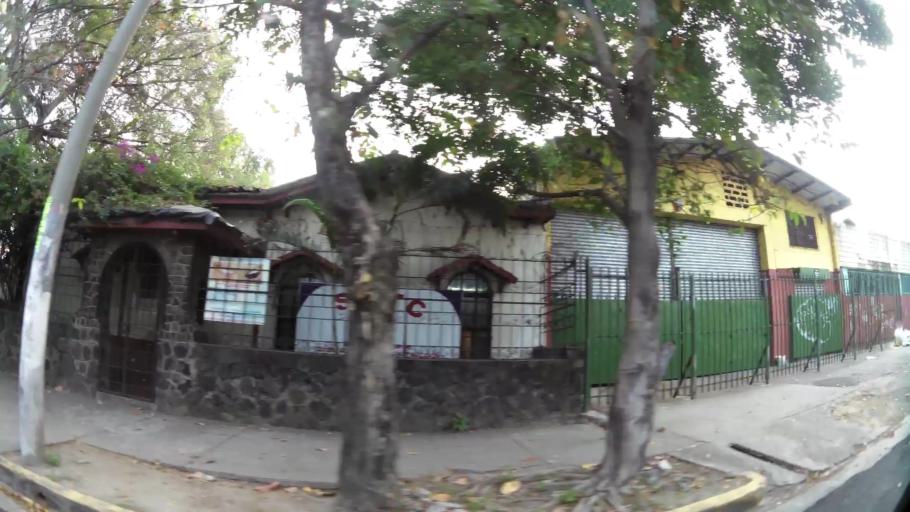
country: SV
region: San Salvador
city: San Salvador
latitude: 13.7061
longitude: -89.1907
